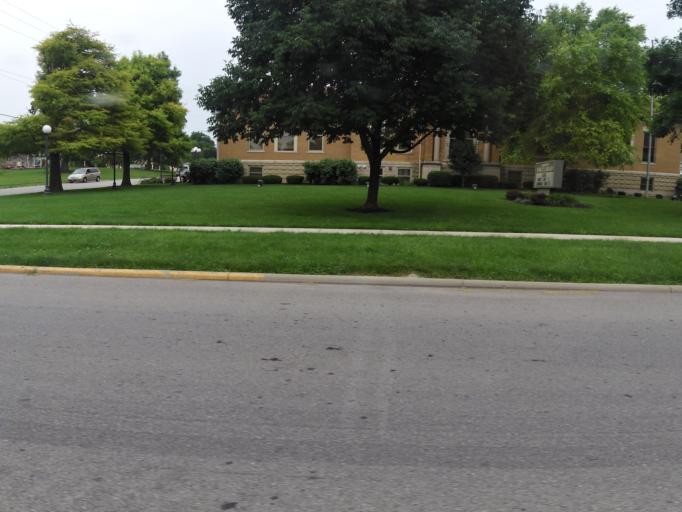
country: US
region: Ohio
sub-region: Clinton County
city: Wilmington
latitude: 39.4492
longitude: -83.8284
